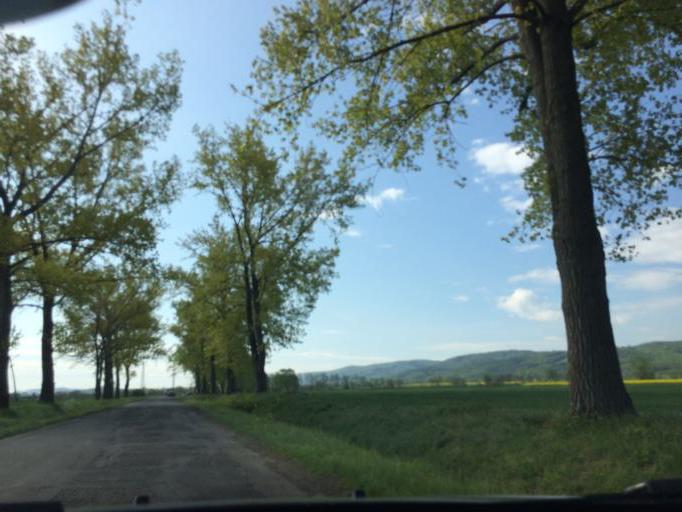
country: PL
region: Lower Silesian Voivodeship
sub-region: Powiat dzierzoniowski
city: Pieszyce
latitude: 50.7435
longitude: 16.5549
